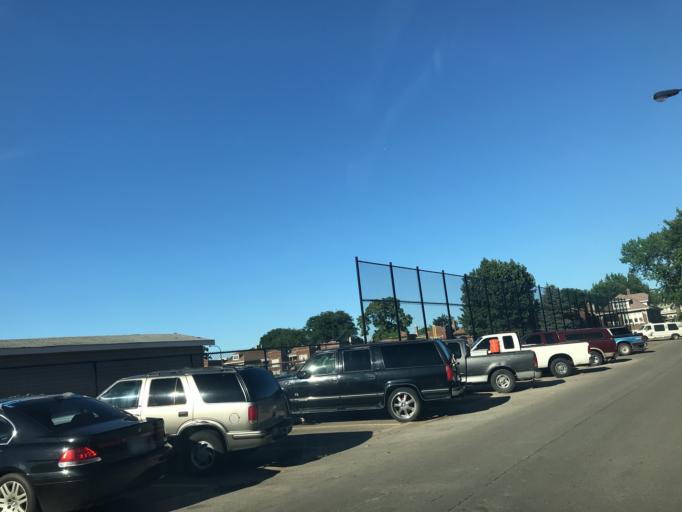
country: US
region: Illinois
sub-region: Cook County
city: Cicero
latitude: 41.8454
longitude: -87.7711
